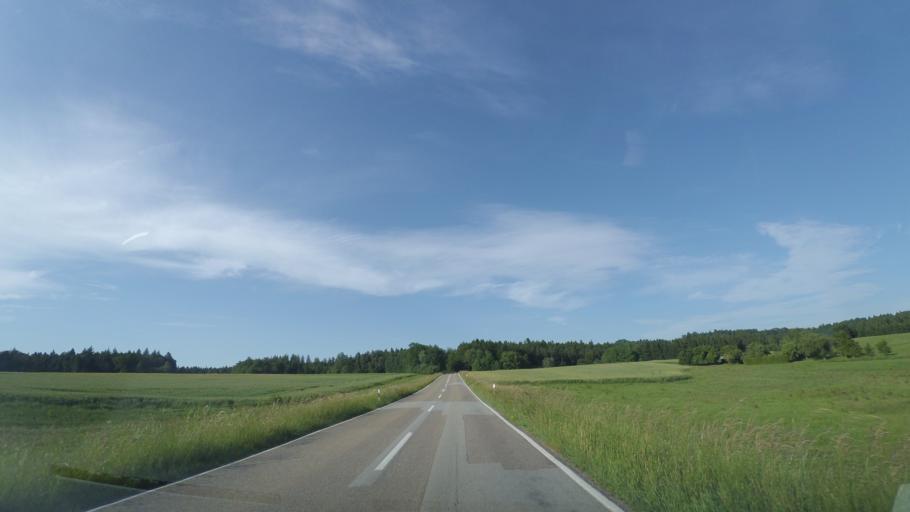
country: DE
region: Baden-Wuerttemberg
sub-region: Regierungsbezirk Stuttgart
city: Gschwend
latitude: 48.9184
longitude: 9.7059
